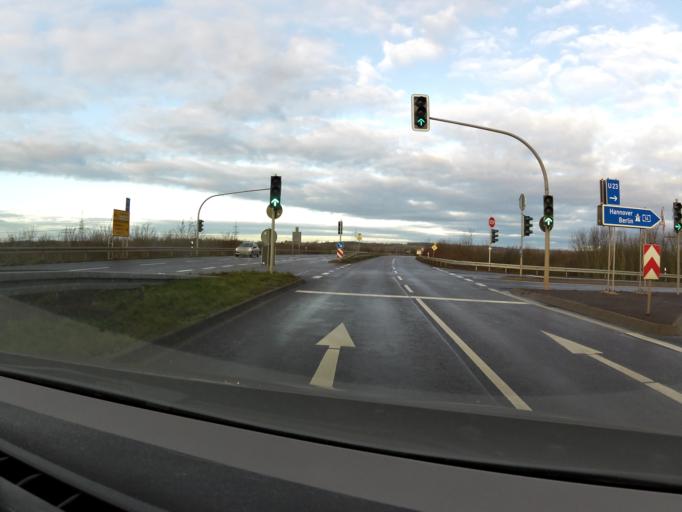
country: DE
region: Saxony-Anhalt
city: Diesdorf
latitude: 52.1434
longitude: 11.5432
